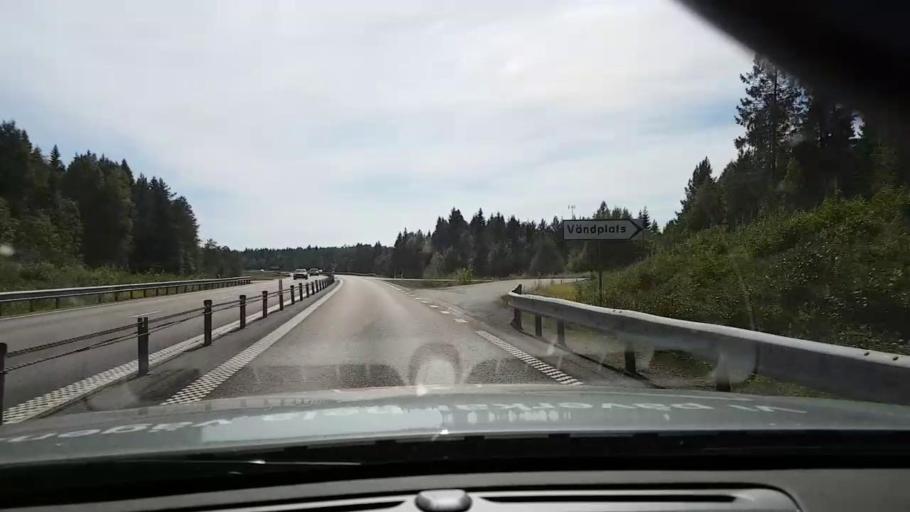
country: SE
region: Vaesternorrland
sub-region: OErnskoeldsviks Kommun
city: Husum
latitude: 63.3951
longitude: 19.1958
